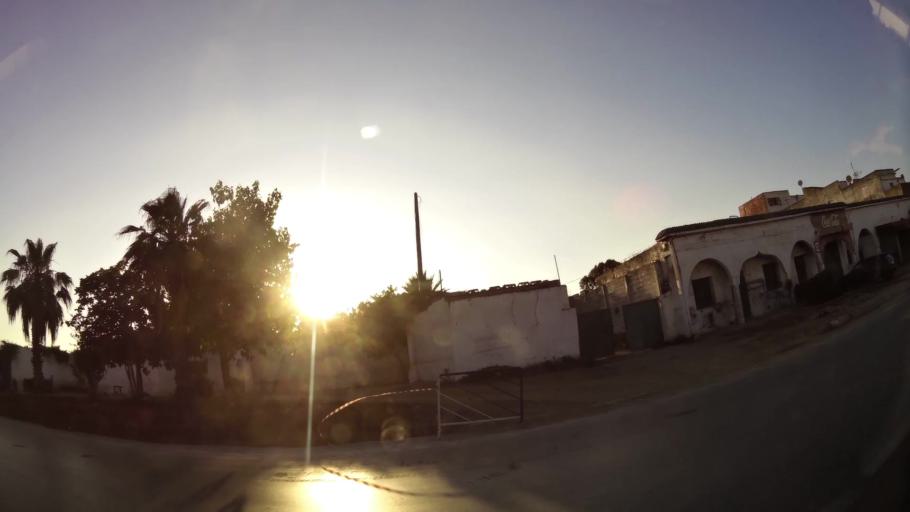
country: MA
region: Rabat-Sale-Zemmour-Zaer
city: Sale
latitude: 34.1179
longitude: -6.7434
